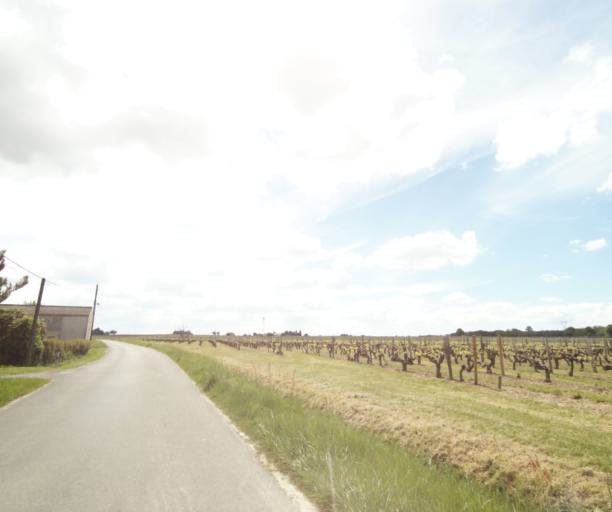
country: FR
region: Poitou-Charentes
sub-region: Departement de la Charente-Maritime
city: Burie
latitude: 45.7442
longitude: -0.4524
